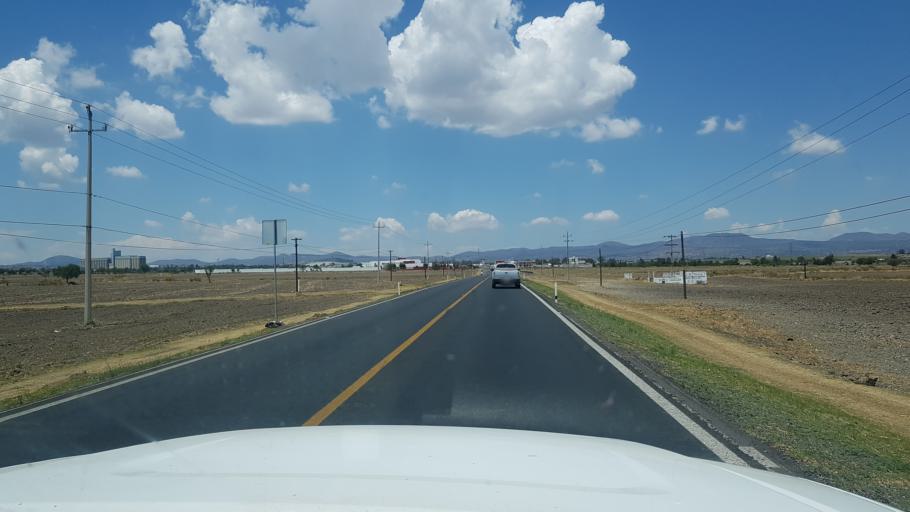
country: MX
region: Hidalgo
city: Calpulalpan
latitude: 19.5809
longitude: -98.5298
